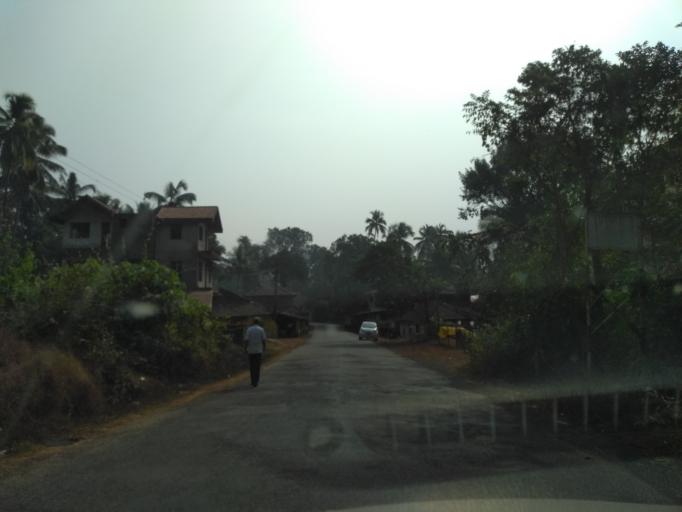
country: IN
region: Maharashtra
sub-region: Sindhudurg
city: Savantvadi
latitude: 15.8196
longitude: 73.8958
